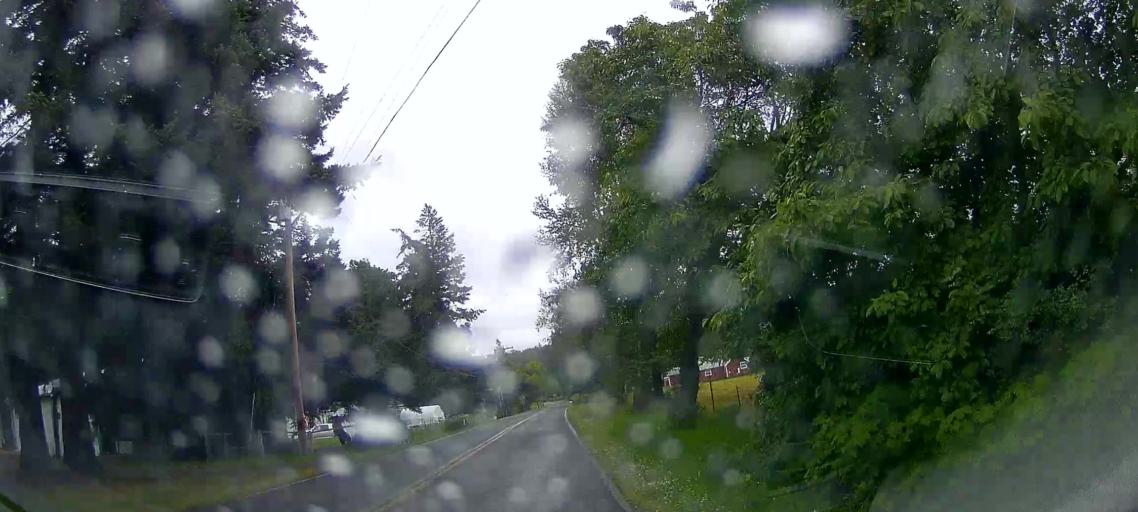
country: US
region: Washington
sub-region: Whatcom County
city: Marietta-Alderwood
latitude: 48.8080
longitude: -122.5684
